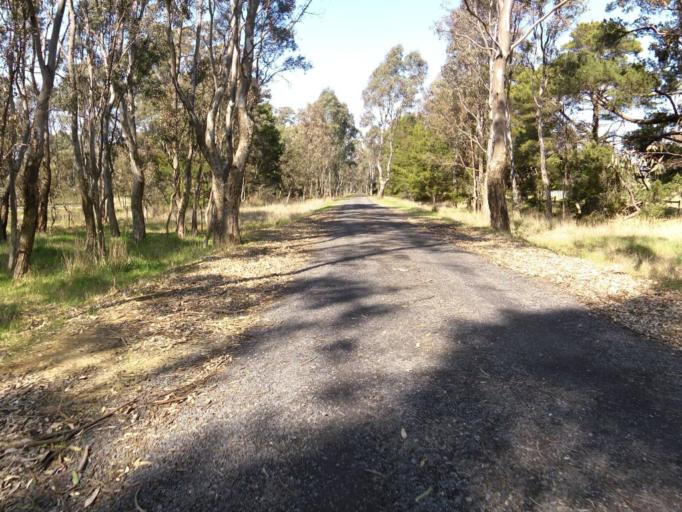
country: AU
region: Victoria
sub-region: Murrindindi
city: Alexandra
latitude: -36.9861
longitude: 145.7311
